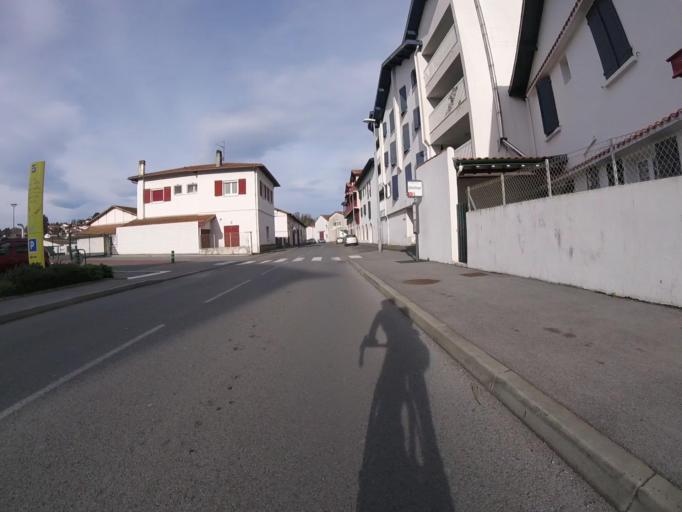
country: FR
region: Aquitaine
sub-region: Departement des Pyrenees-Atlantiques
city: Saint-Jean-de-Luz
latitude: 43.3815
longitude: -1.6647
